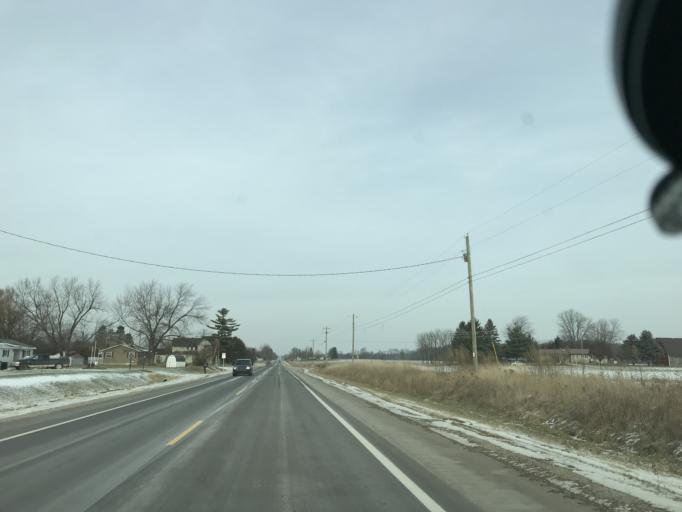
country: US
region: Michigan
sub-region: Ionia County
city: Lake Odessa
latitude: 42.7838
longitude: -85.0743
